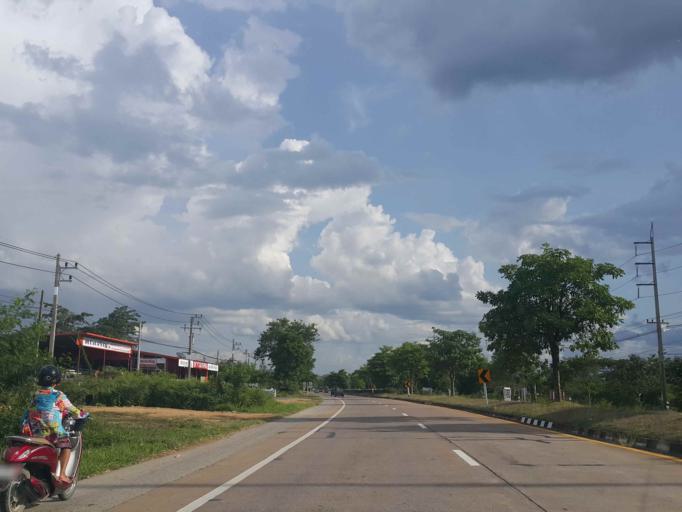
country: TH
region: Phrae
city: Sung Men
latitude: 18.0121
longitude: 100.1061
